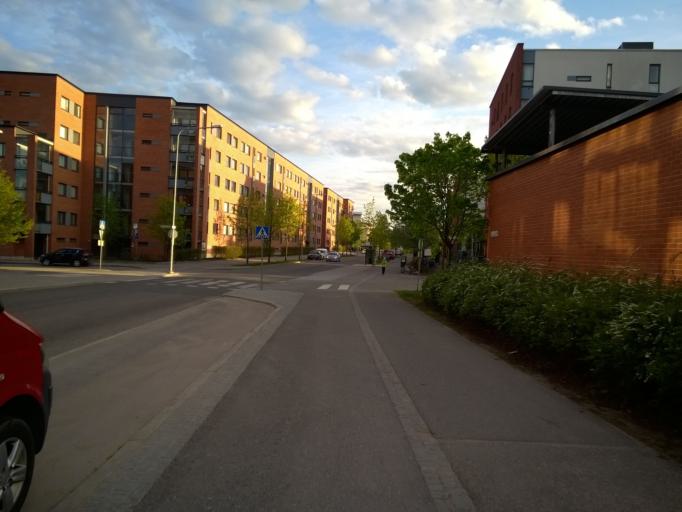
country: FI
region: Uusimaa
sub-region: Helsinki
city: Vantaa
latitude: 60.2312
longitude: 25.0303
